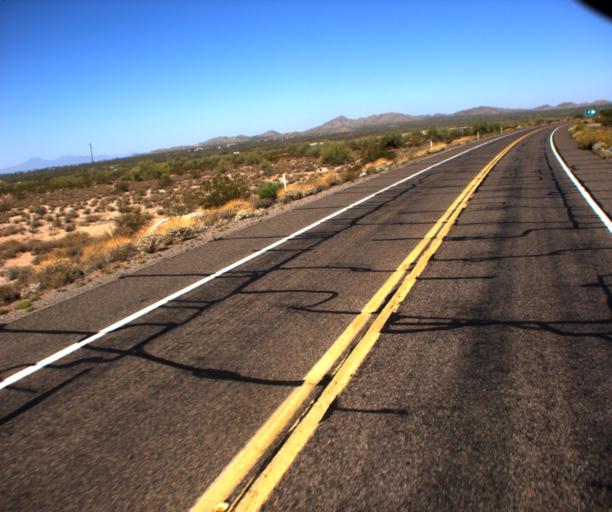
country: US
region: Arizona
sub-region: Pinal County
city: Sacaton
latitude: 33.0031
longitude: -111.7416
